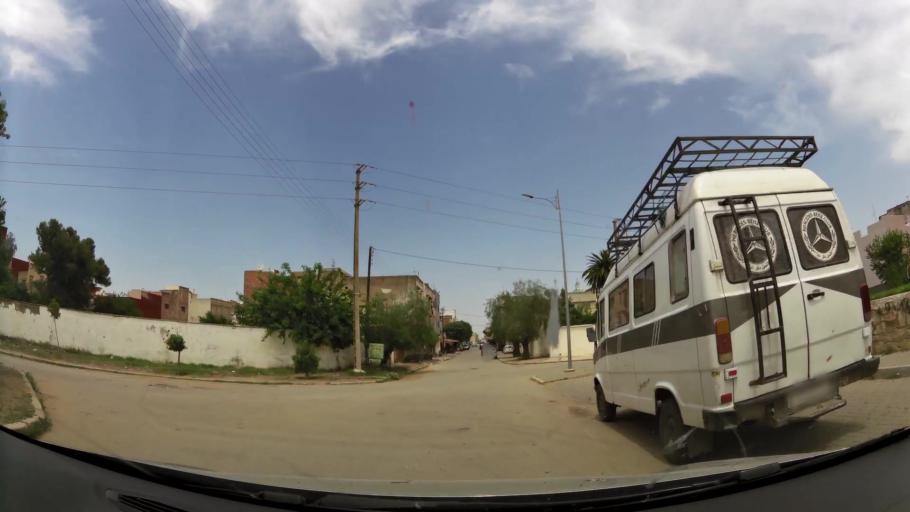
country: MA
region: Rabat-Sale-Zemmour-Zaer
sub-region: Khemisset
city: Khemisset
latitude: 33.8227
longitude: -6.0669
